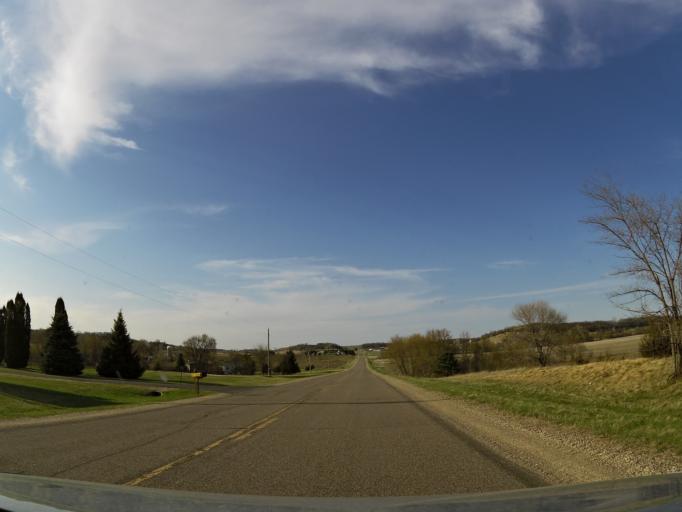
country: US
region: Wisconsin
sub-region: Pierce County
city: River Falls
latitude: 44.7596
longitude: -92.6396
